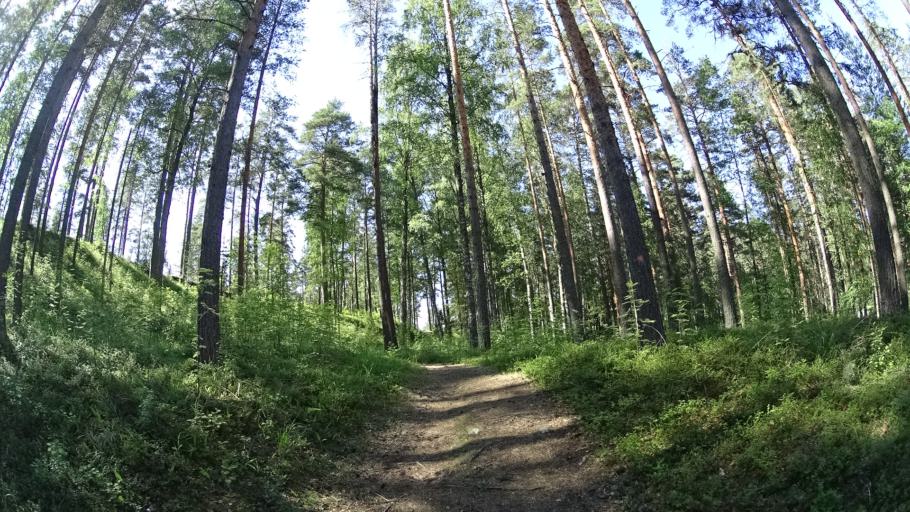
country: FI
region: Southern Savonia
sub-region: Savonlinna
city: Punkaharju
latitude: 61.7994
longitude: 29.3098
